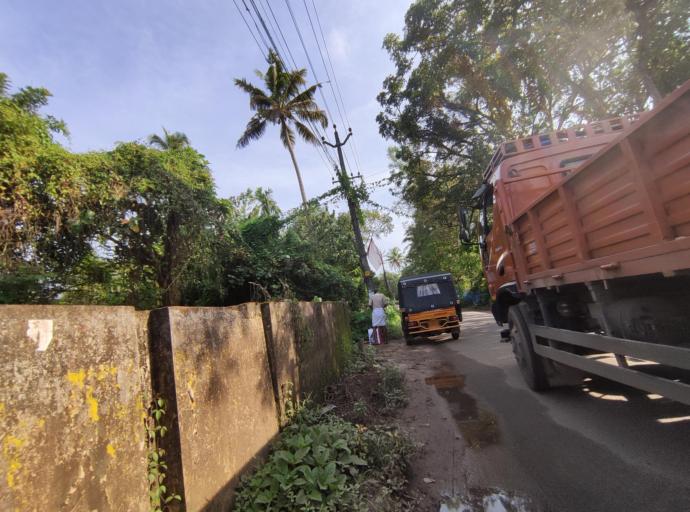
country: IN
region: Kerala
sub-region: Alappuzha
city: Vayalar
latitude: 9.6962
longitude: 76.3376
